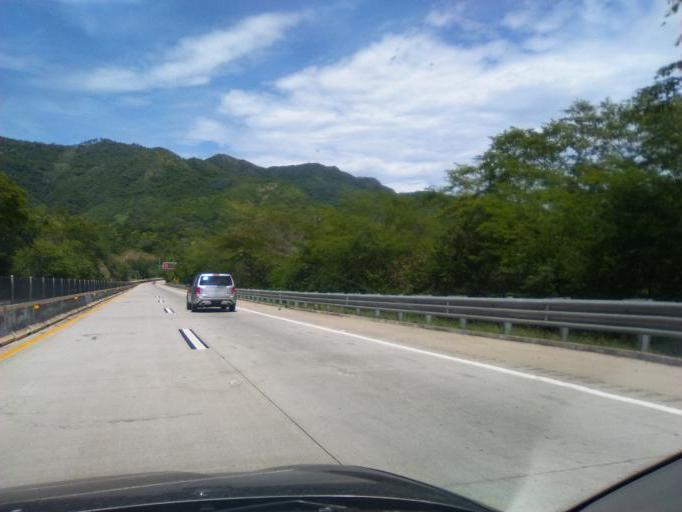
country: MX
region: Guerrero
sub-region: Acapulco de Juarez
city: Pueblo Madero (El Playon)
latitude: 17.0968
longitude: -99.5933
